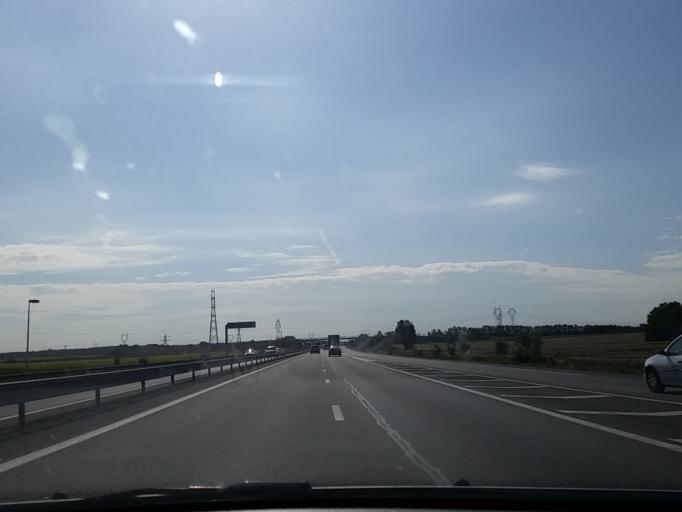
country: FR
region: Centre
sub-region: Departement du Cher
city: Marmagne
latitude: 47.0940
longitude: 2.2443
